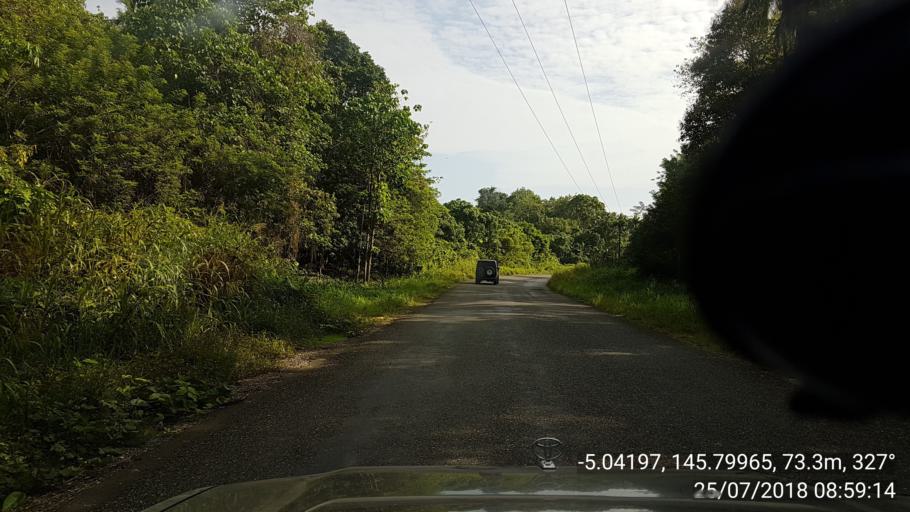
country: PG
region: Madang
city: Madang
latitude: -5.0414
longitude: 145.7996
